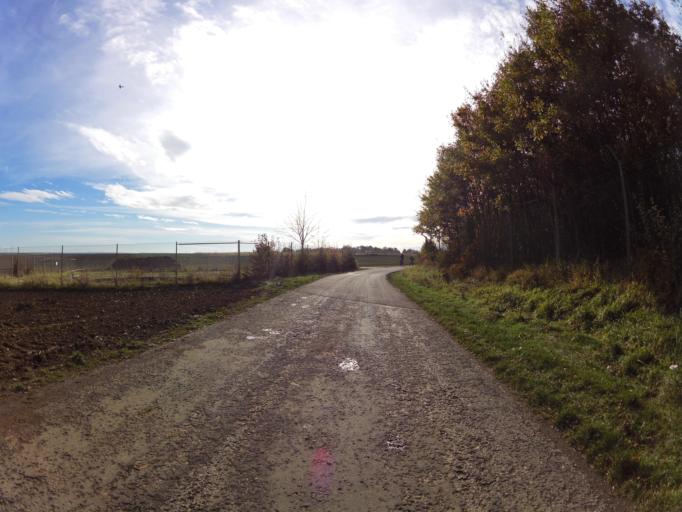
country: DE
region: Bavaria
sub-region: Regierungsbezirk Unterfranken
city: Gaukonigshofen
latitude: 49.6534
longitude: 9.9835
